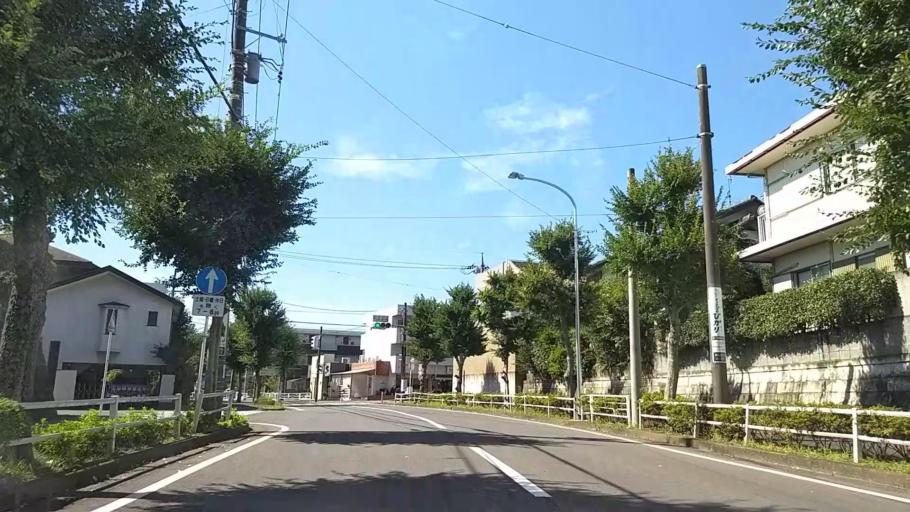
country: JP
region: Tokyo
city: Chofugaoka
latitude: 35.5828
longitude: 139.5517
